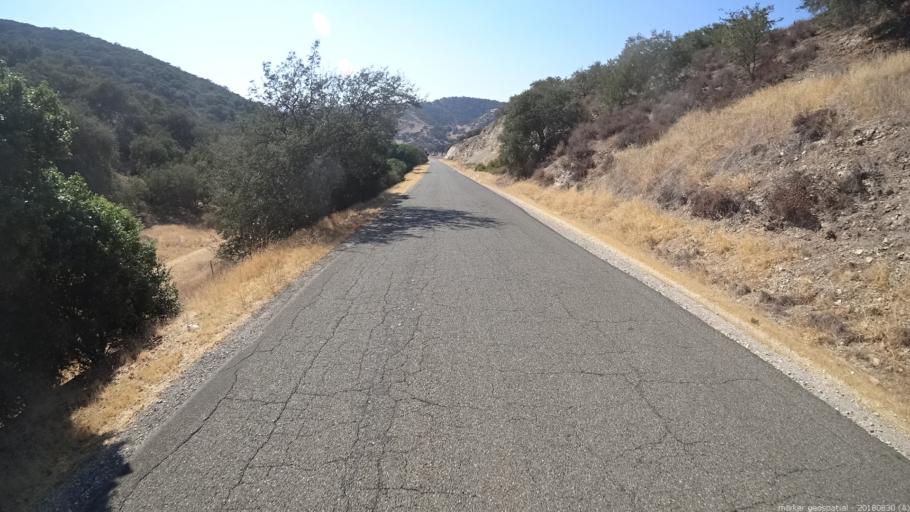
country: US
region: California
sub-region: Monterey County
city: King City
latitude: 36.1141
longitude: -121.1213
